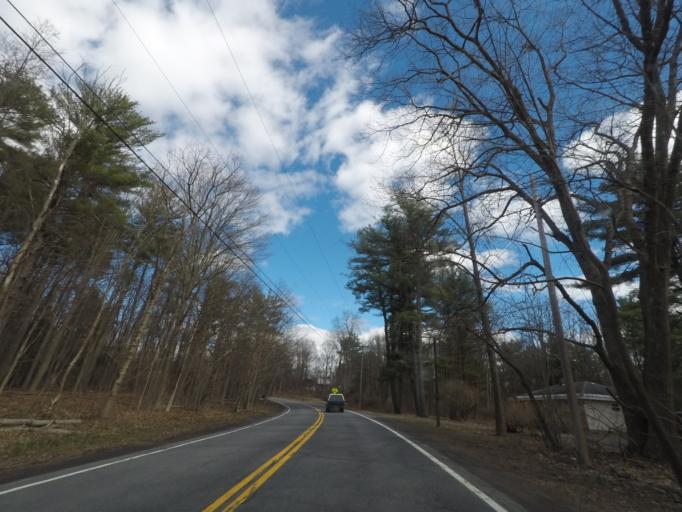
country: US
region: New York
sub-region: Albany County
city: Delmar
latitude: 42.5689
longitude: -73.8944
